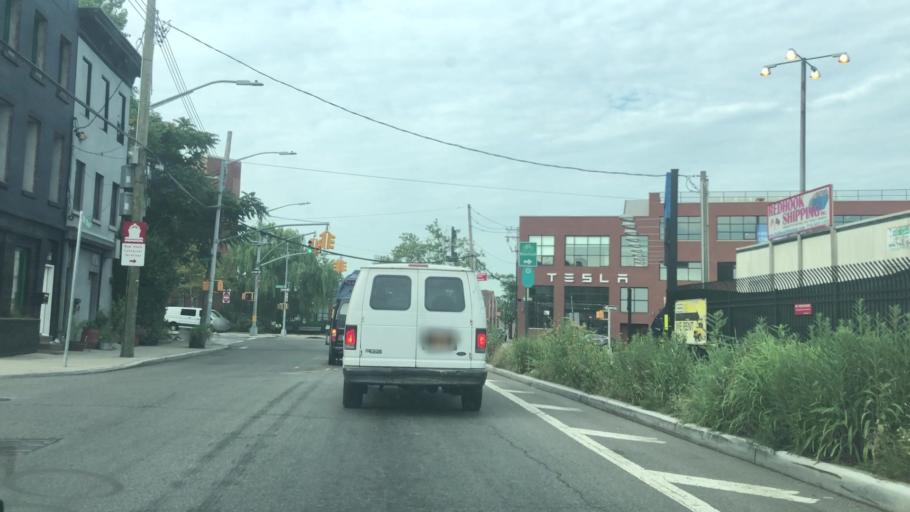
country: US
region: New York
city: New York City
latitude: 40.6838
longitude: -74.0058
